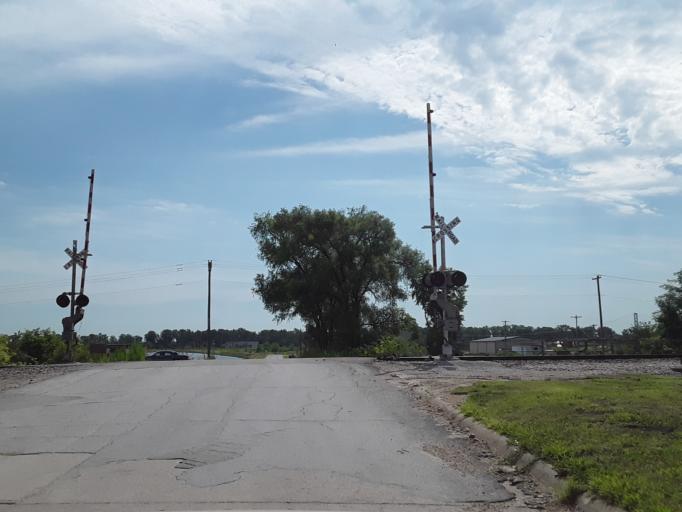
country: US
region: Nebraska
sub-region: Cass County
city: Plattsmouth
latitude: 41.0112
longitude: -95.8814
